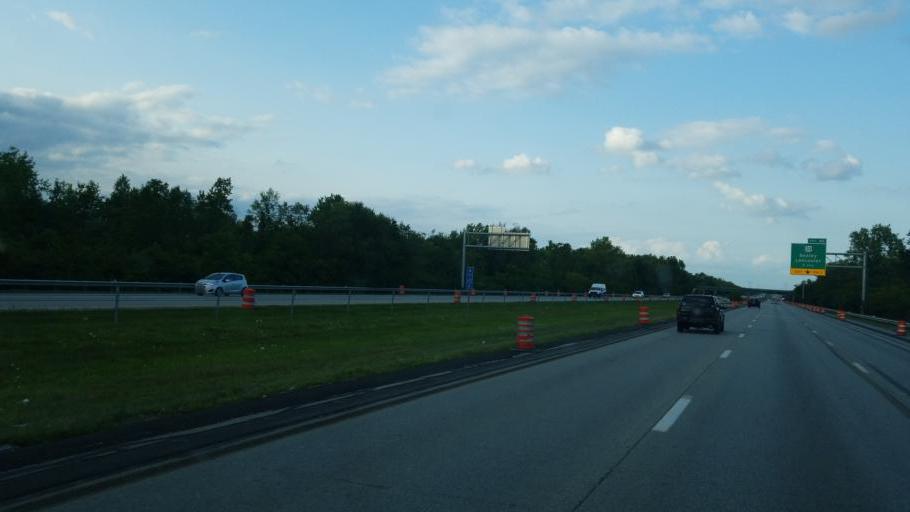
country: US
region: Ohio
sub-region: Franklin County
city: Groveport
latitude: 39.8851
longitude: -82.9149
